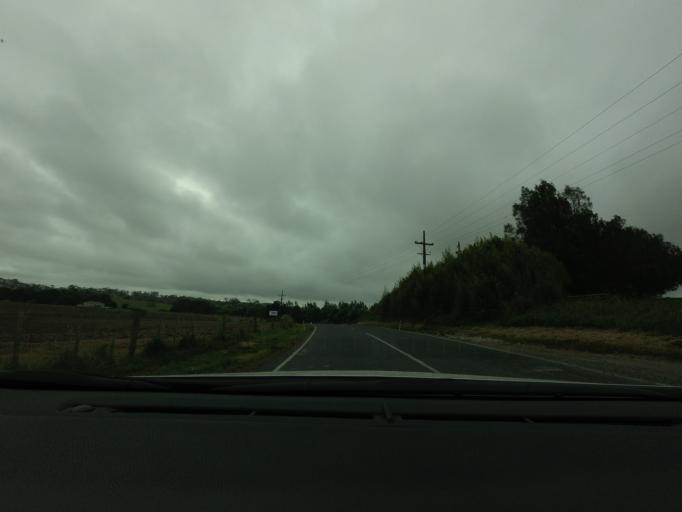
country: NZ
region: Auckland
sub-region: Auckland
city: Wellsford
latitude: -36.2816
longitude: 174.5703
